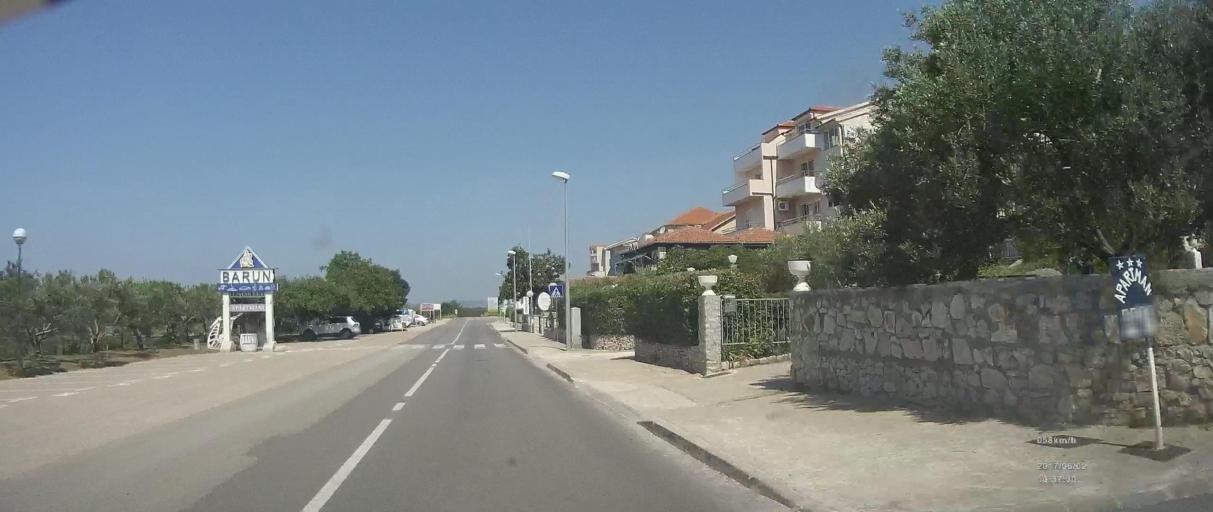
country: HR
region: Sibensko-Kniniska
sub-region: Grad Sibenik
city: Sibenik
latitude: 43.7005
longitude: 15.8973
